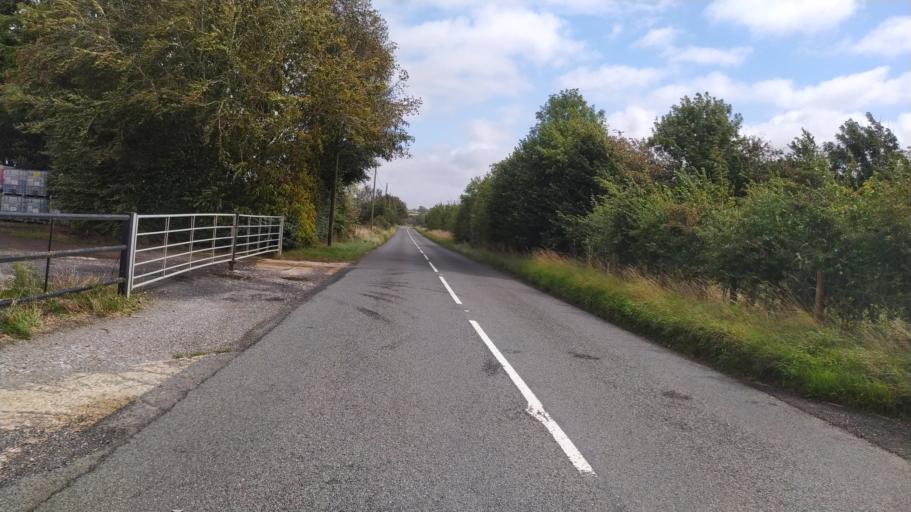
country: GB
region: England
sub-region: Wiltshire
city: Bower Chalke
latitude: 50.9561
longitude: -2.0249
